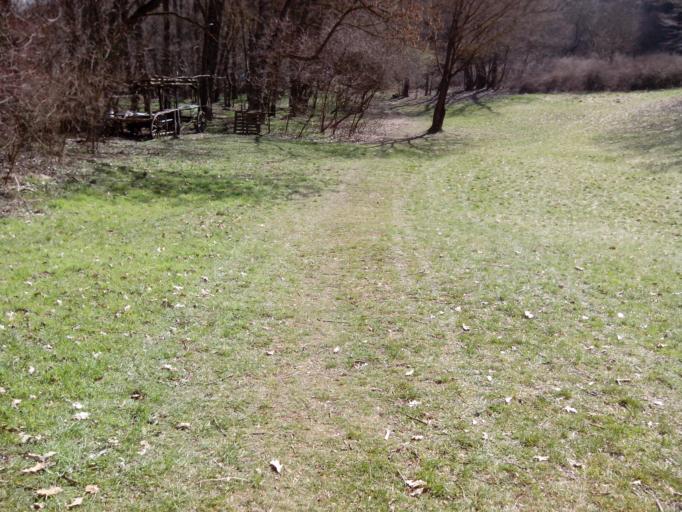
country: CZ
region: Central Bohemia
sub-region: Okres Beroun
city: Beroun
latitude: 49.9319
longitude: 14.1247
